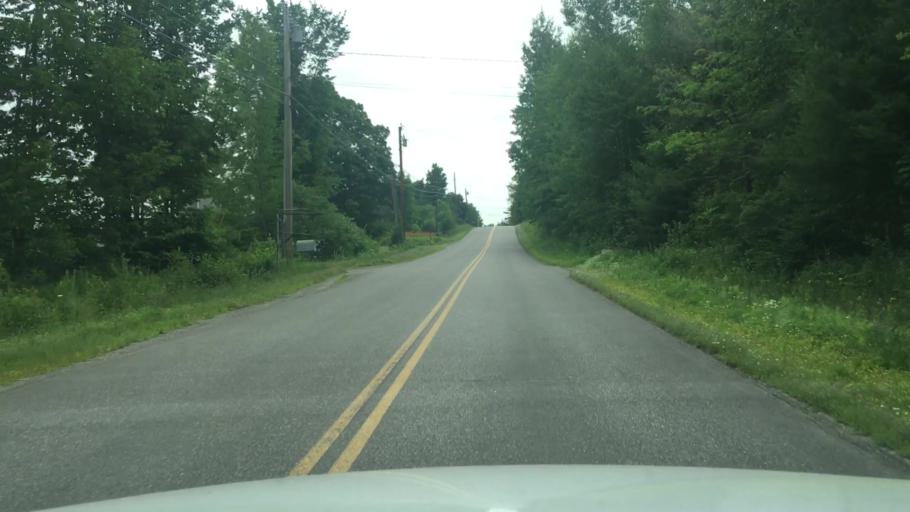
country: US
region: Maine
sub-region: Kennebec County
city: Benton
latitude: 44.5815
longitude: -69.5024
